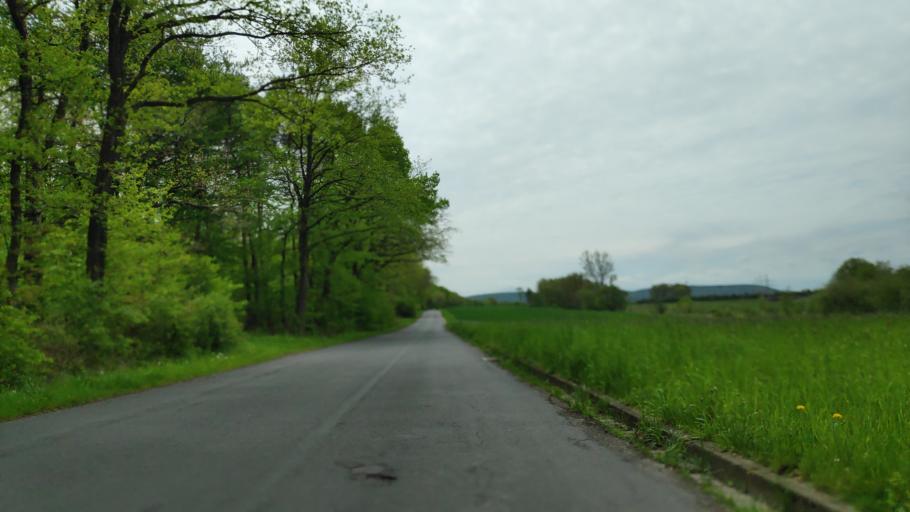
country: DE
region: Lower Saxony
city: Buckeburg
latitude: 52.3050
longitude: 8.9925
